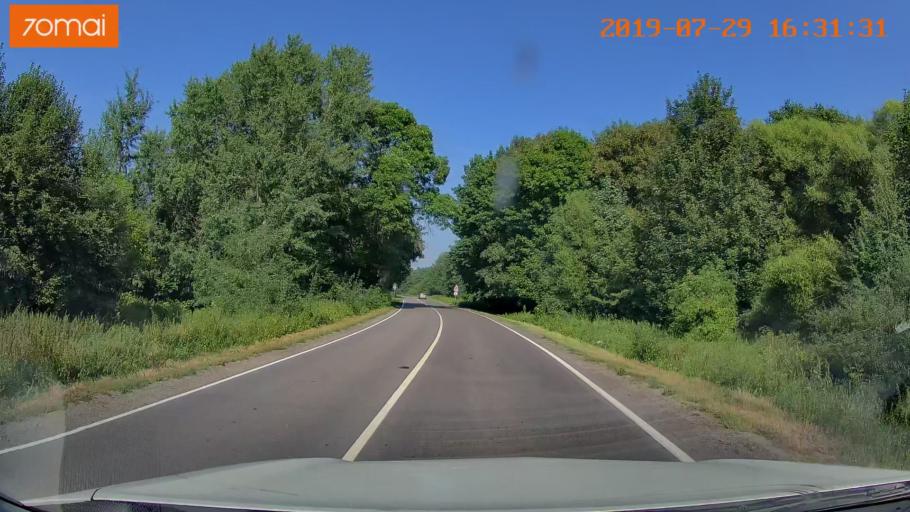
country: RU
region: Kaliningrad
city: Primorsk
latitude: 54.7291
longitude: 20.0146
